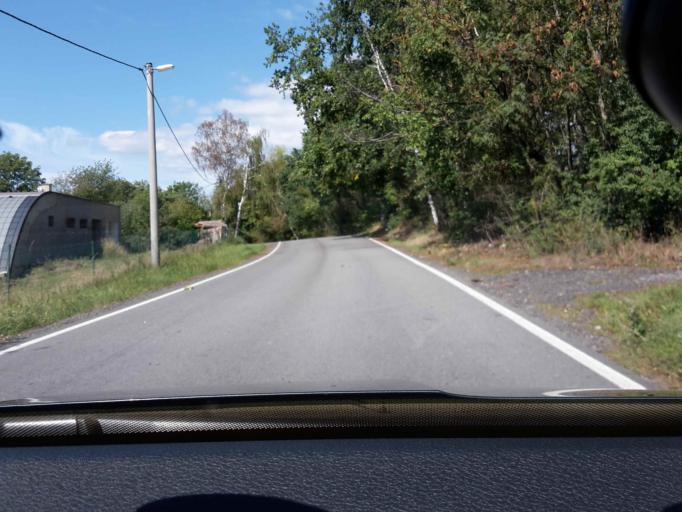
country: CZ
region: Vysocina
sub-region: Okres Jihlava
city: Telc
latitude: 49.1644
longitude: 15.5031
